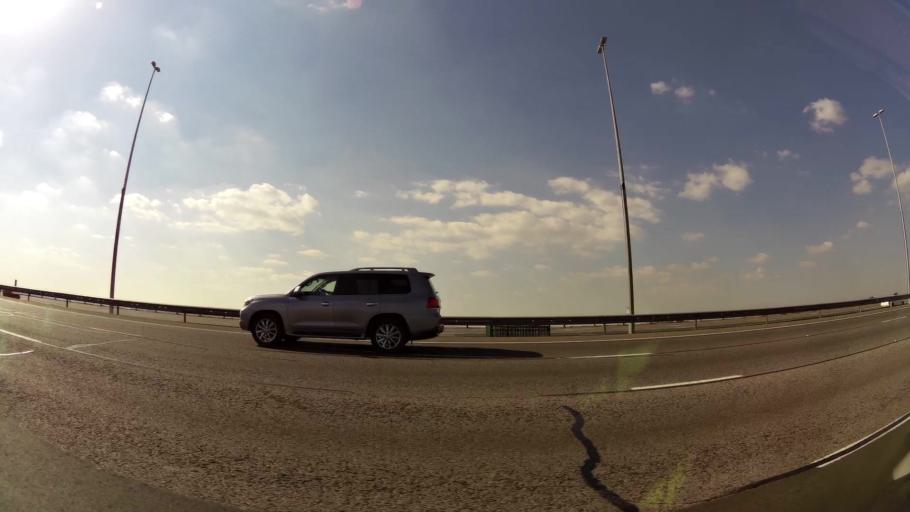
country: ZA
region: Gauteng
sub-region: Ekurhuleni Metropolitan Municipality
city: Tembisa
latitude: -26.0553
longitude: 28.2810
